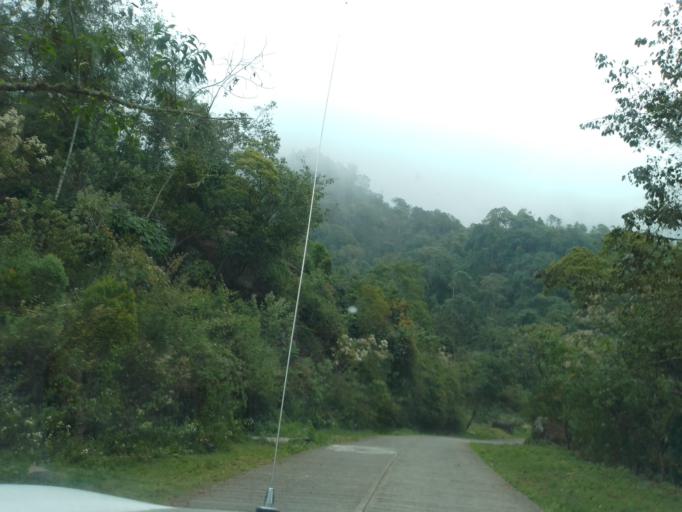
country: MX
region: Chiapas
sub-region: Union Juarez
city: Santo Domingo
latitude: 15.0928
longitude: -92.0951
